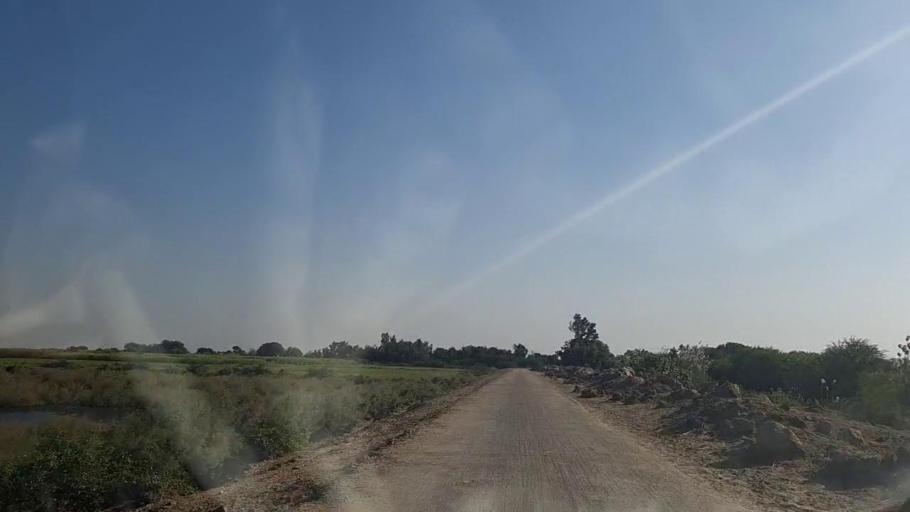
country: PK
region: Sindh
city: Mirpur Batoro
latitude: 24.5556
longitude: 68.1719
